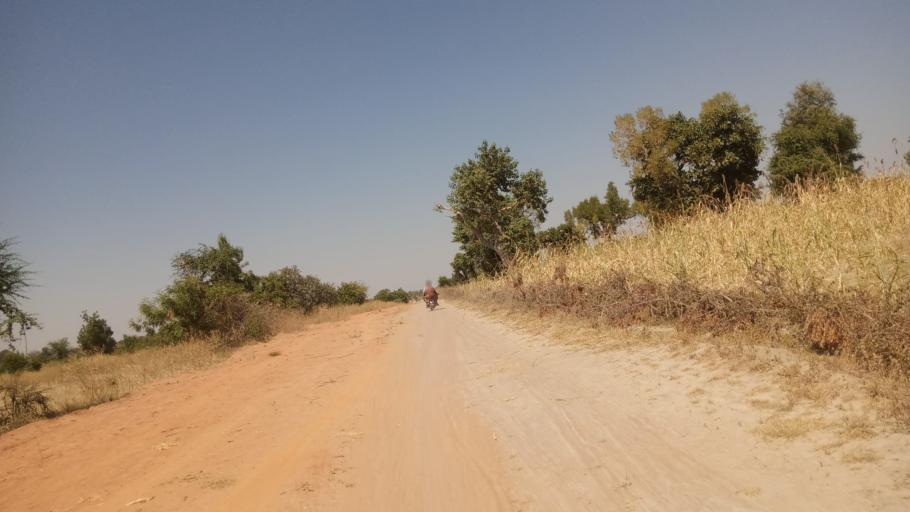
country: NG
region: Adamawa
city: Mayo Belwa
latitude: 9.0871
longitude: 12.0269
